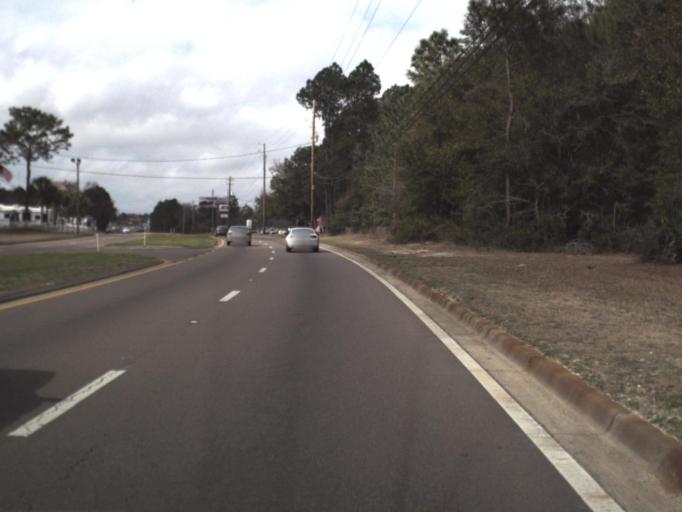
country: US
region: Florida
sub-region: Bay County
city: Springfield
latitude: 30.1748
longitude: -85.5960
